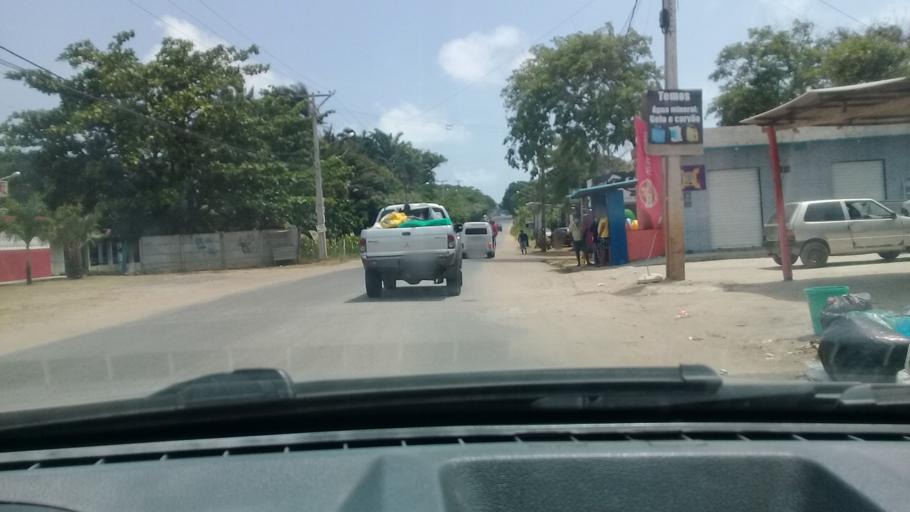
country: BR
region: Pernambuco
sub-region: Itamaraca
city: Itamaraca
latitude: -7.7860
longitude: -34.8398
